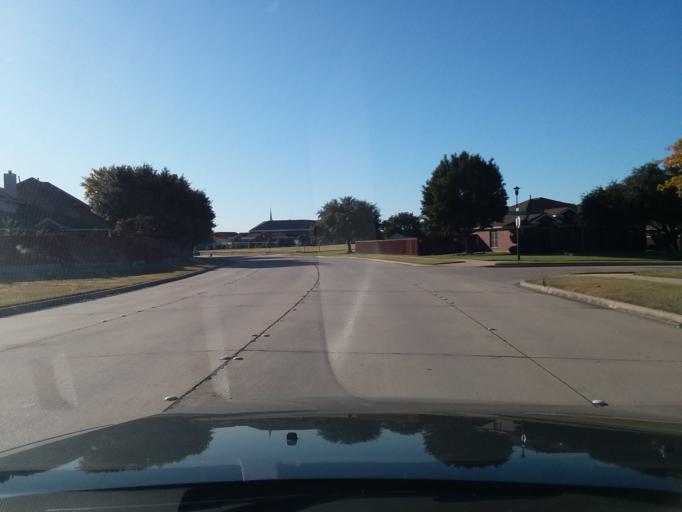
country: US
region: Texas
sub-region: Denton County
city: Highland Village
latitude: 33.0614
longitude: -97.0275
